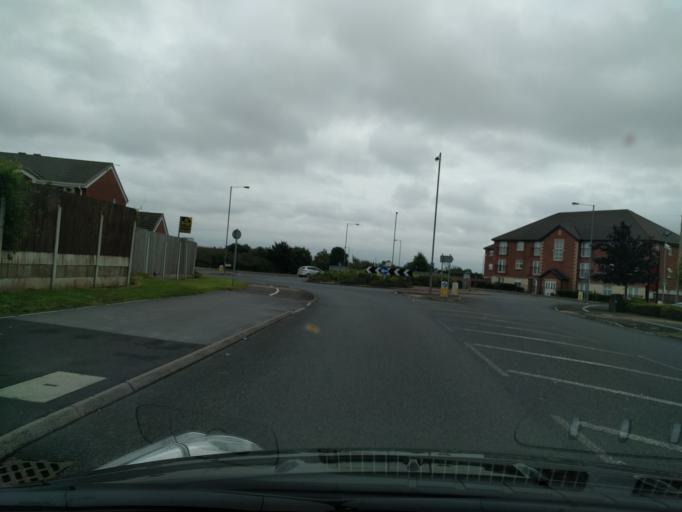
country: GB
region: England
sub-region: St. Helens
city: Haydock
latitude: 53.4715
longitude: -2.6643
